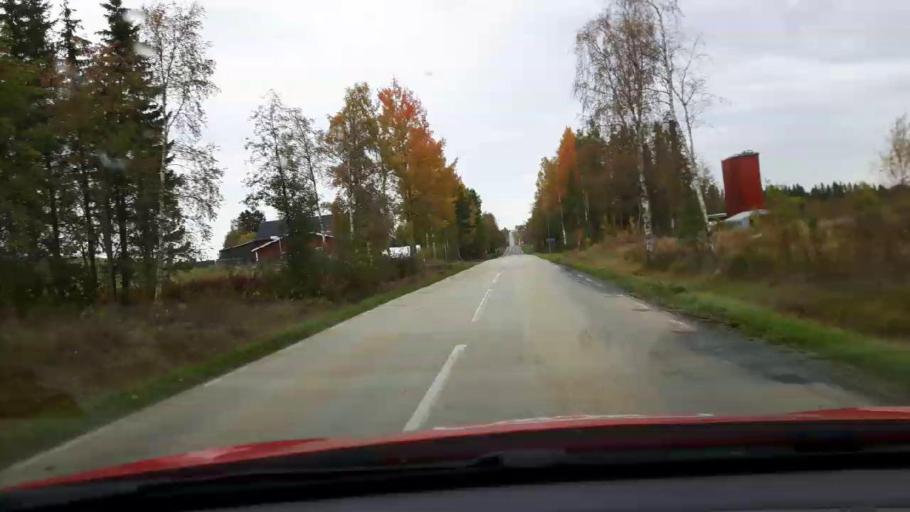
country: SE
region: Jaemtland
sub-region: Bergs Kommun
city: Hoverberg
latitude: 62.9930
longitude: 14.3394
